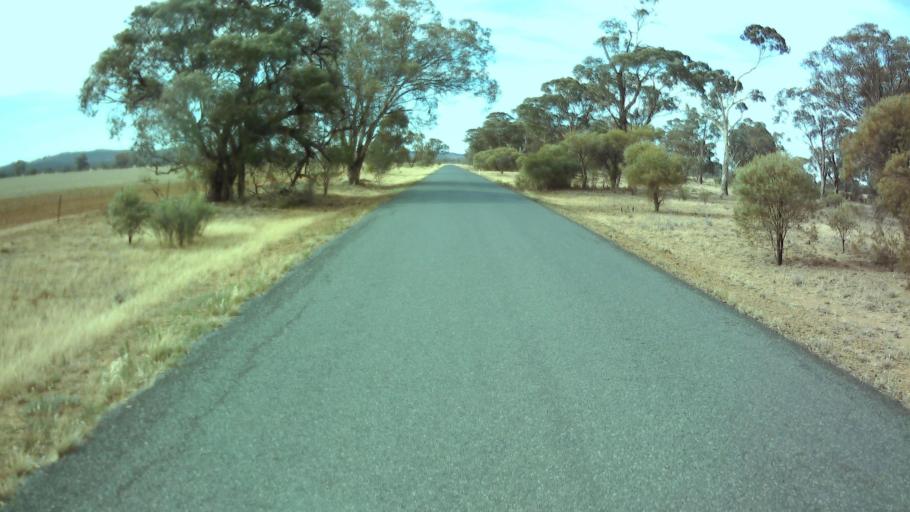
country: AU
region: New South Wales
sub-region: Weddin
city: Grenfell
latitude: -33.8630
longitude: 147.8595
